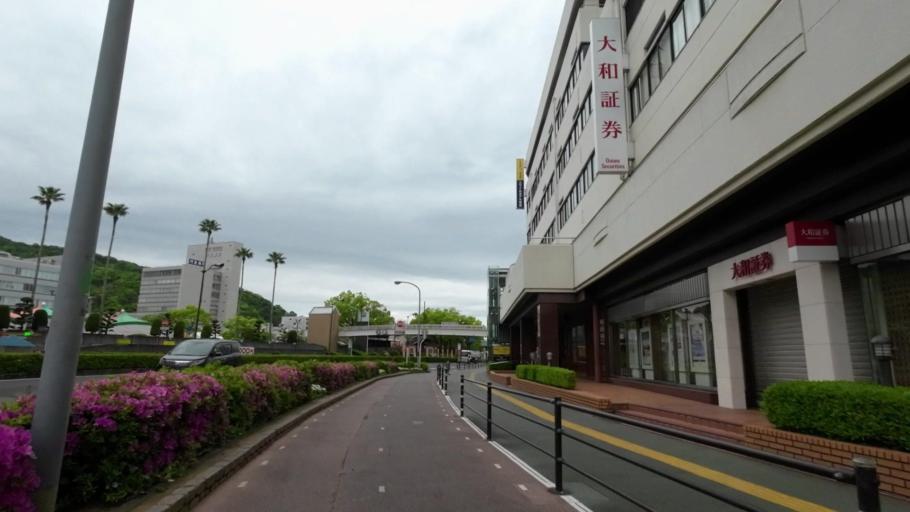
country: JP
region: Tokushima
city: Tokushima-shi
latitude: 34.0730
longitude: 134.5490
